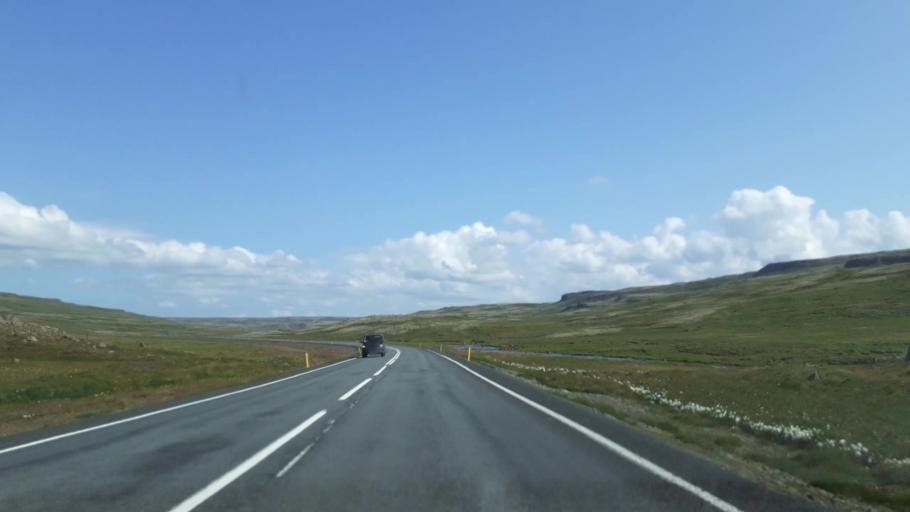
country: IS
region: West
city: Borgarnes
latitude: 64.9171
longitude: -21.1338
